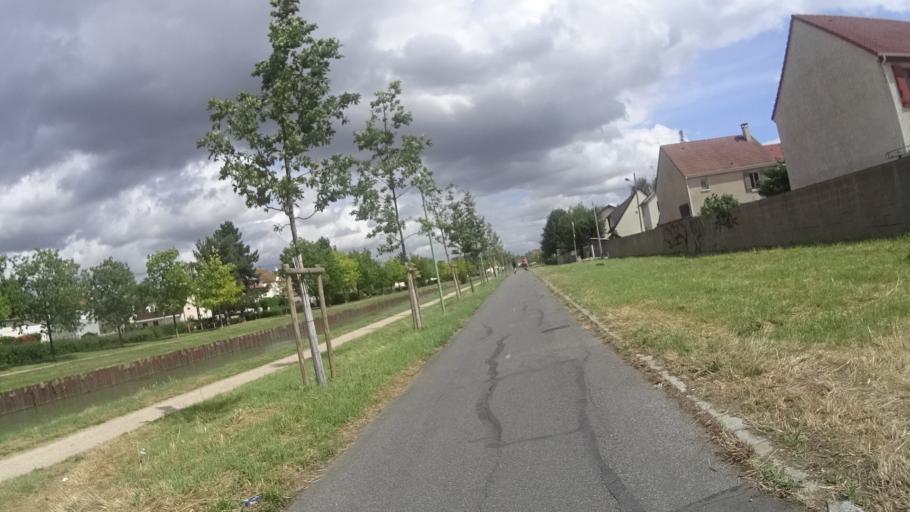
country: FR
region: Ile-de-France
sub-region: Departement de Seine-Saint-Denis
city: Sevran
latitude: 48.9295
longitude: 2.5189
